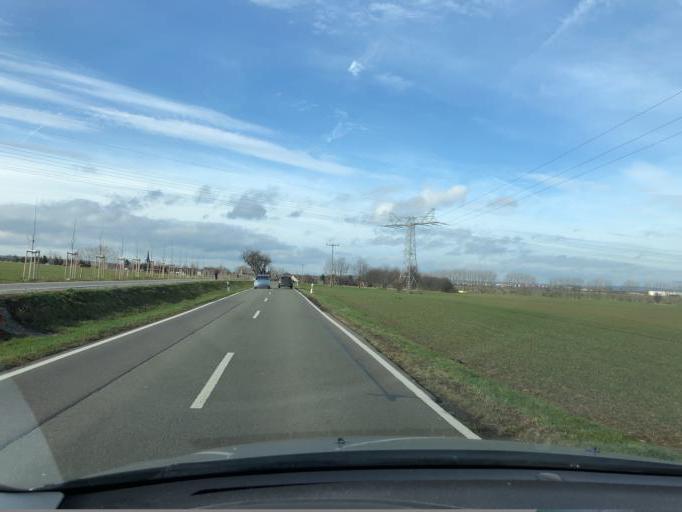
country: DE
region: Thuringia
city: Kleinmolsen
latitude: 50.9919
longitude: 11.1169
